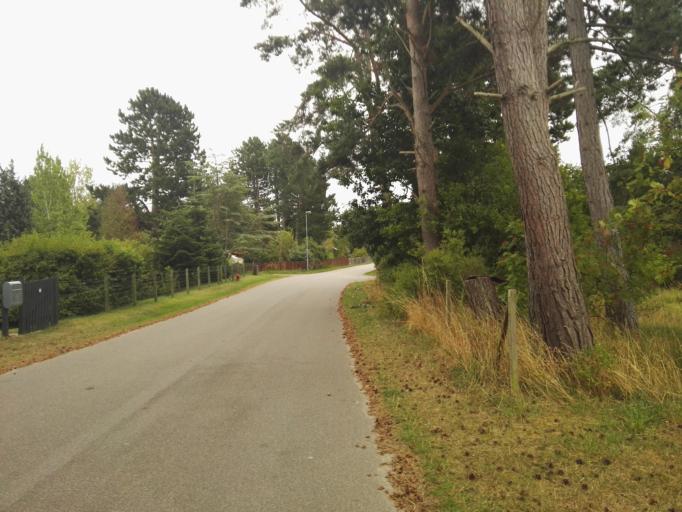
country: DK
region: Zealand
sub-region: Odsherred Kommune
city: Nykobing Sjaelland
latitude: 55.9356
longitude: 11.6663
